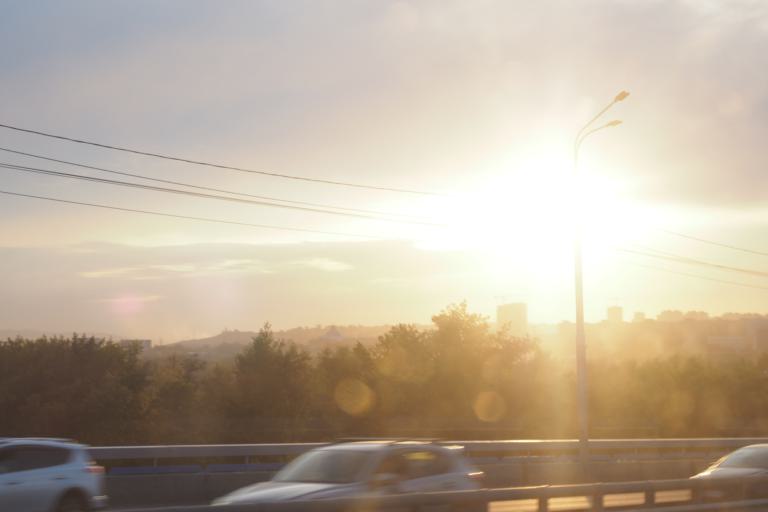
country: RU
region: Krasnoyarskiy
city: Krasnoyarsk
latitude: 56.0217
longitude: 92.9468
